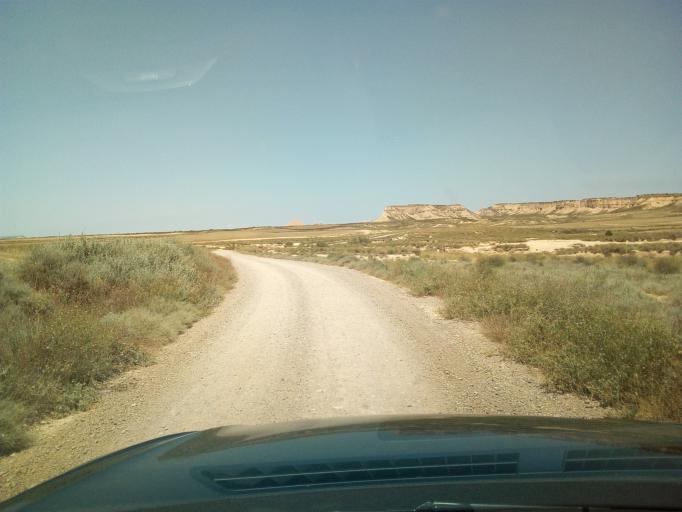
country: ES
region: Aragon
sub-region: Provincia de Zaragoza
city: Sadaba
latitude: 42.1825
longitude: -1.4086
